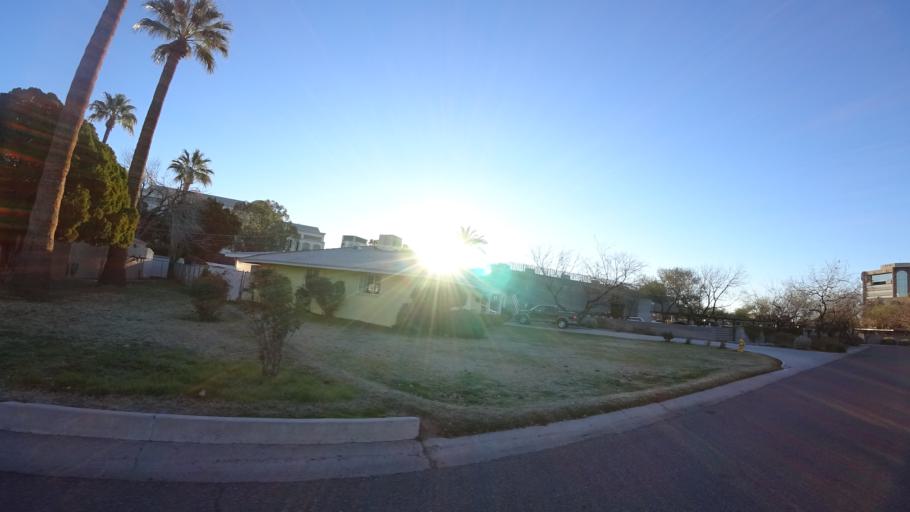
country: US
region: Arizona
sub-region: Maricopa County
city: Paradise Valley
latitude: 33.4825
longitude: -111.9881
